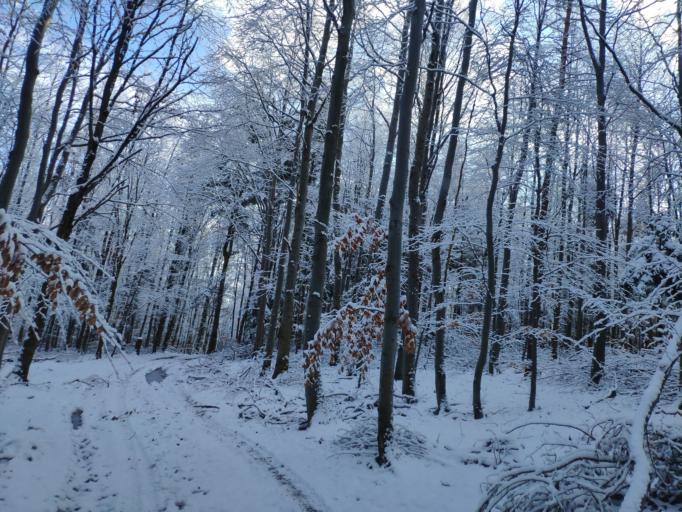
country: SK
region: Kosicky
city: Moldava nad Bodvou
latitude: 48.7457
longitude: 21.0861
